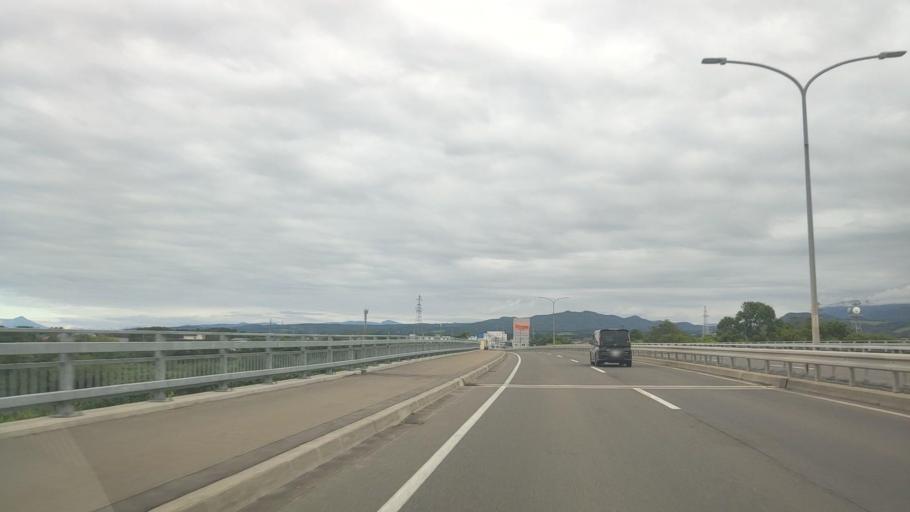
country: JP
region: Hokkaido
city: Nanae
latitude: 42.2641
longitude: 140.2733
